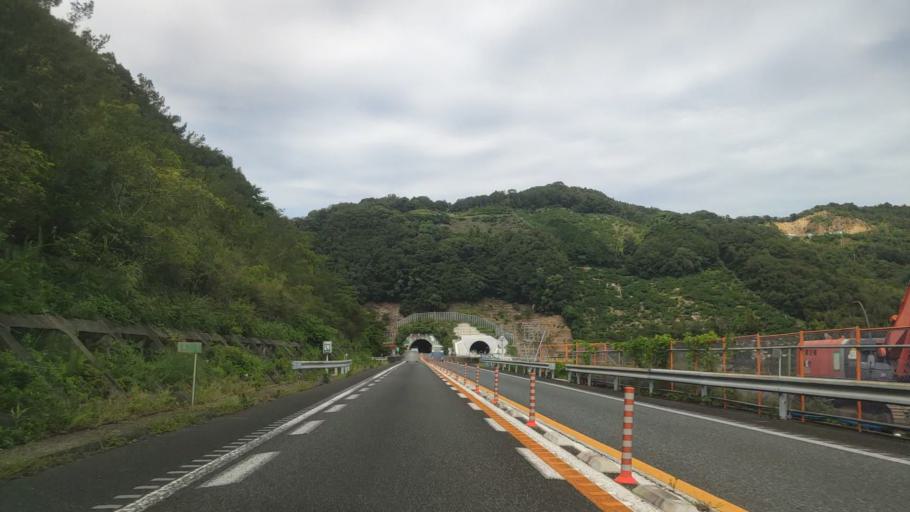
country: JP
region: Wakayama
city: Gobo
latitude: 33.9965
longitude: 135.1971
